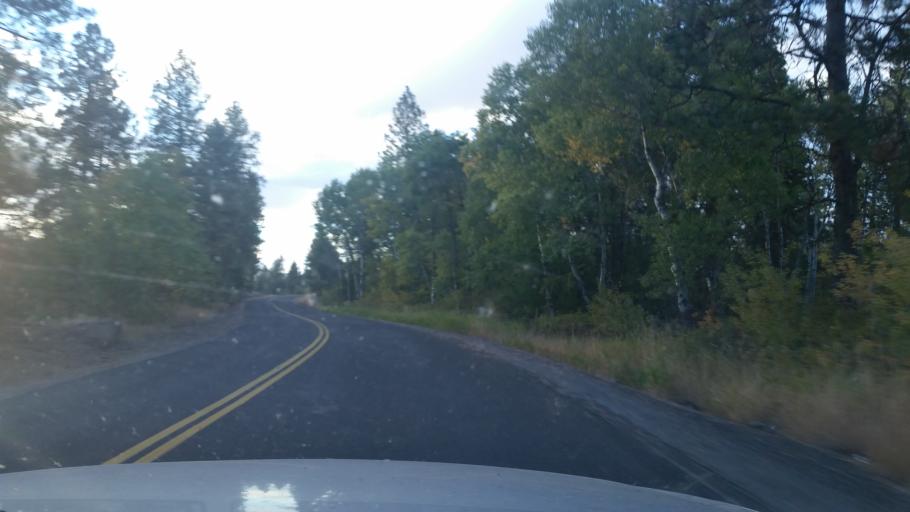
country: US
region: Washington
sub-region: Spokane County
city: Medical Lake
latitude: 47.5448
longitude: -117.6970
